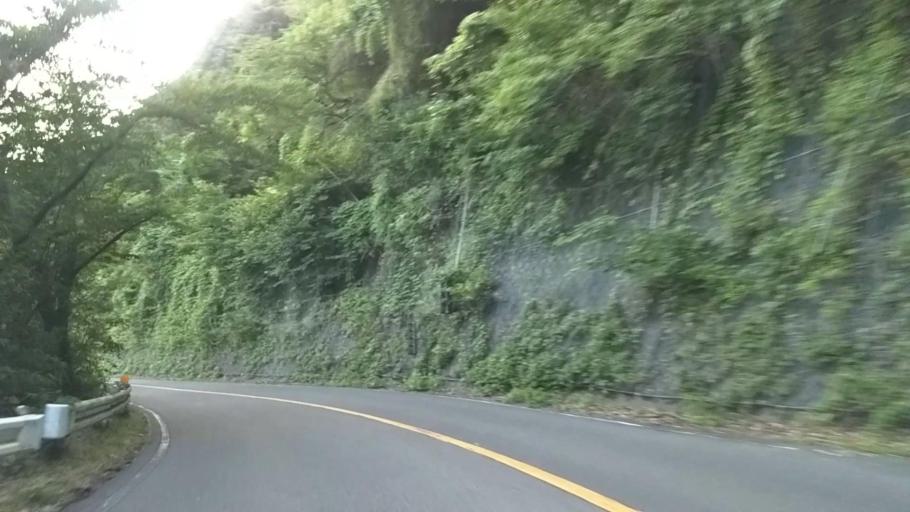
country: JP
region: Tokyo
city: Hachioji
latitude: 35.5958
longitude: 139.2687
